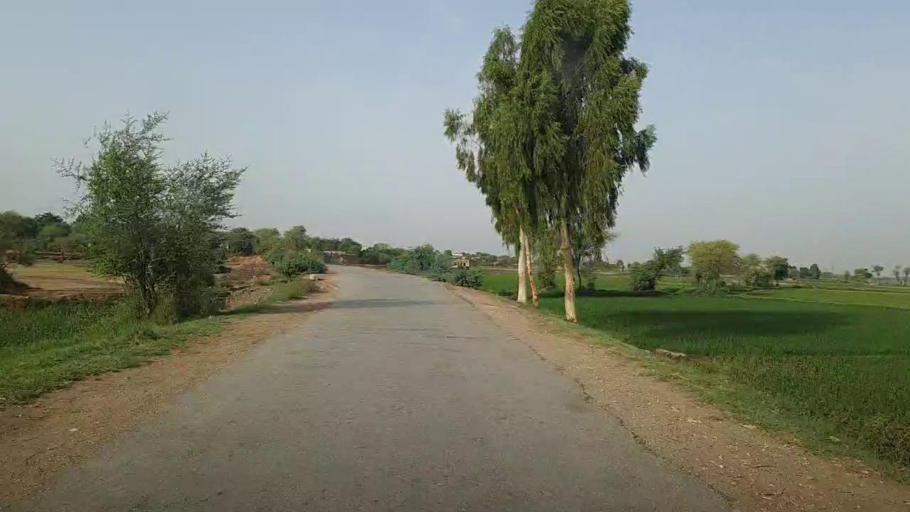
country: PK
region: Sindh
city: Khairpur Nathan Shah
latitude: 27.1196
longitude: 67.7883
